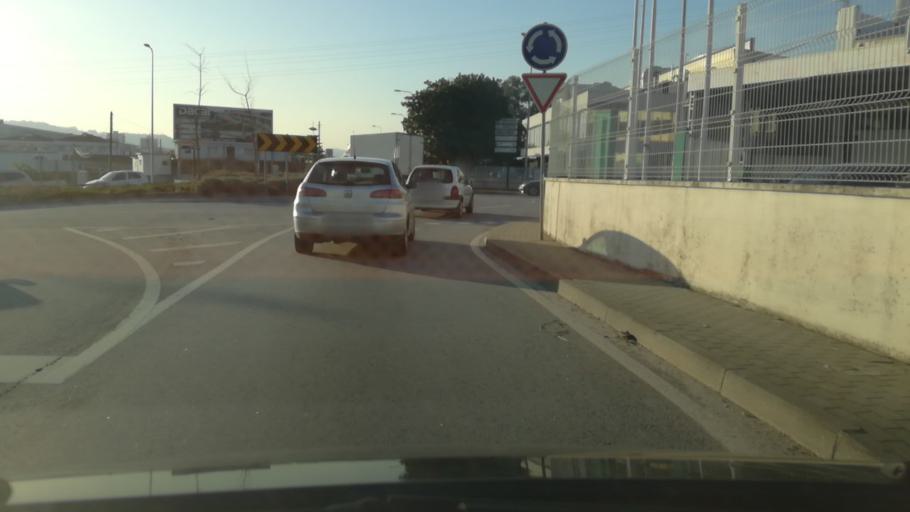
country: PT
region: Porto
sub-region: Trofa
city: Bougado
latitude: 41.3403
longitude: -8.5431
